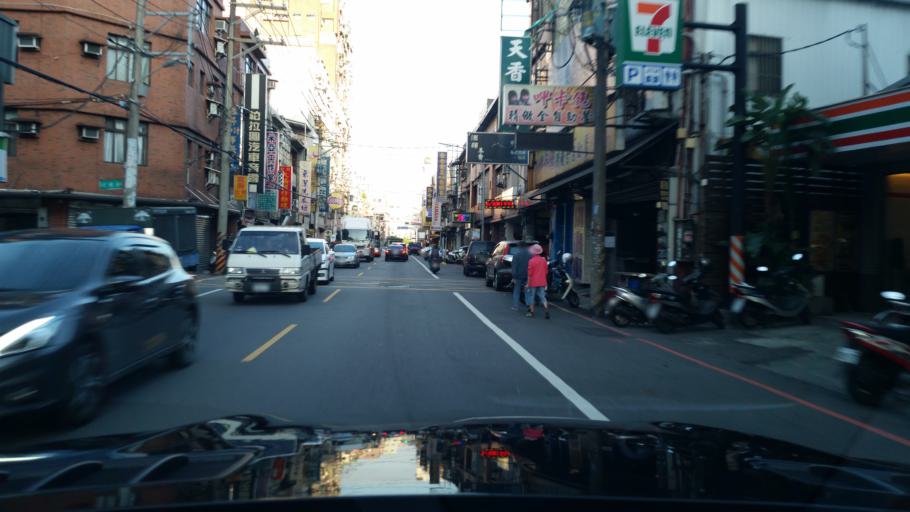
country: TW
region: Taiwan
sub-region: Taoyuan
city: Taoyuan
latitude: 24.9859
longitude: 121.3166
